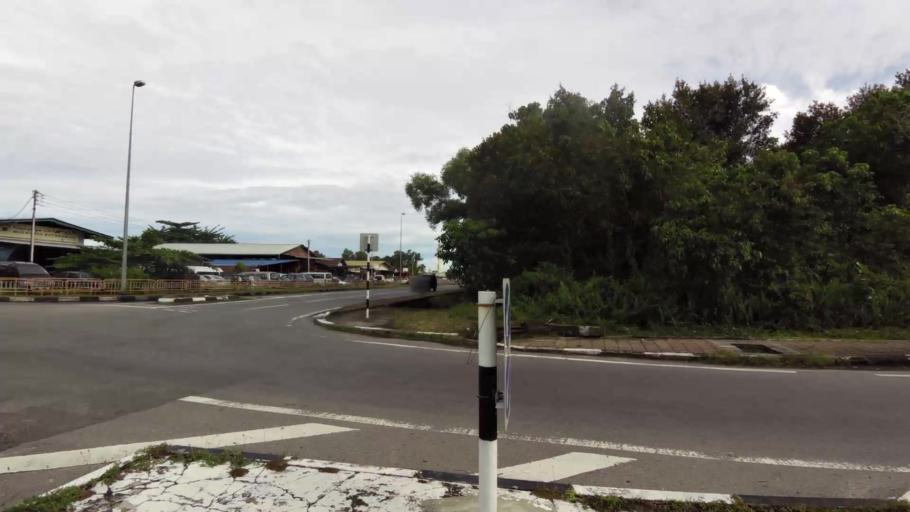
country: BN
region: Belait
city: Seria
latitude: 4.6134
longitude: 114.3348
